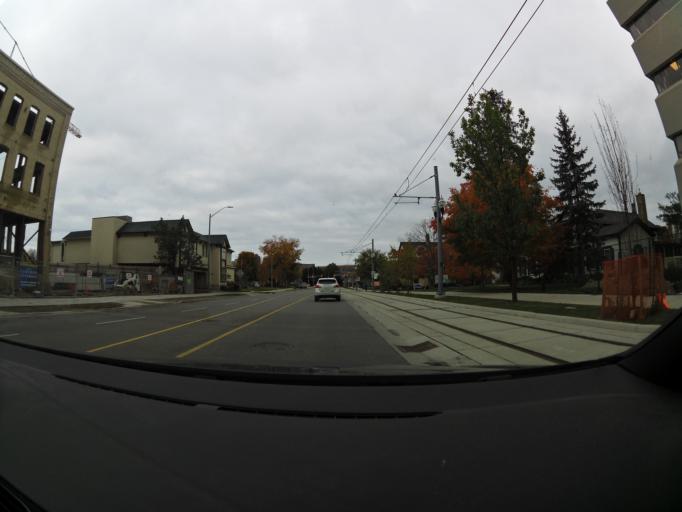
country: CA
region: Ontario
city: Waterloo
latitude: 43.4605
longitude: -80.5195
